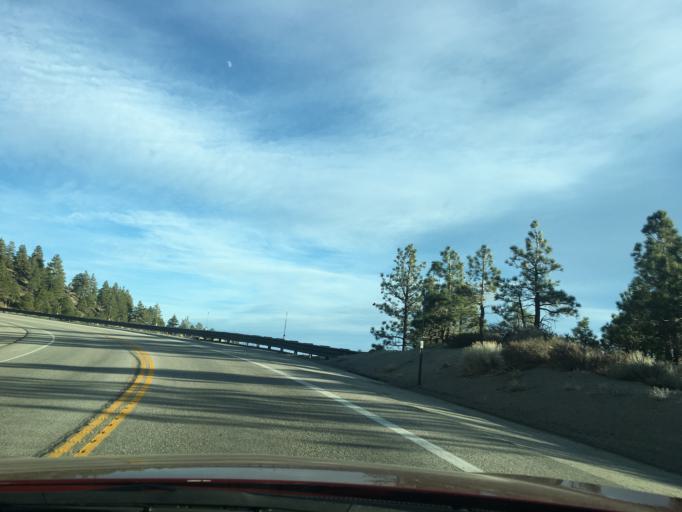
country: US
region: Nevada
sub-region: Douglas County
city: Kingsbury
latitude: 38.9767
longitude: -119.8568
